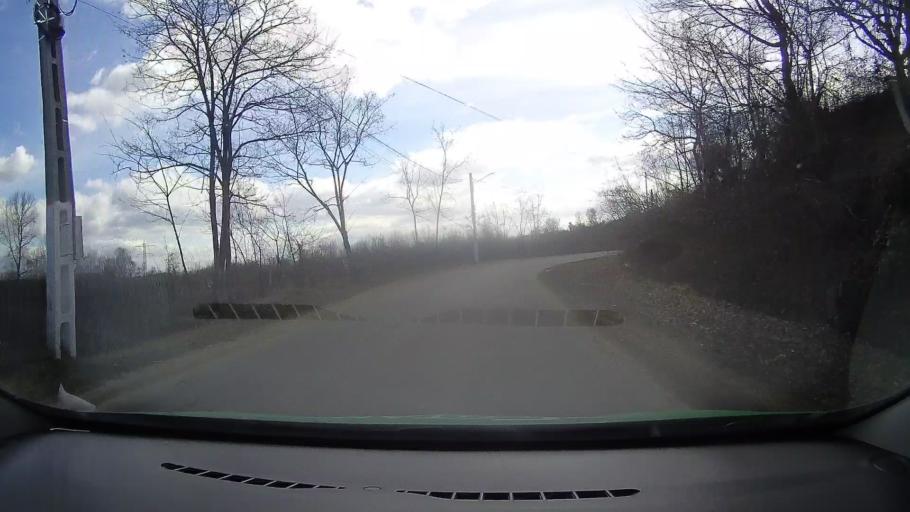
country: RO
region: Dambovita
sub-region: Comuna Sotanga
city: Teis
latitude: 44.9721
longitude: 25.3959
